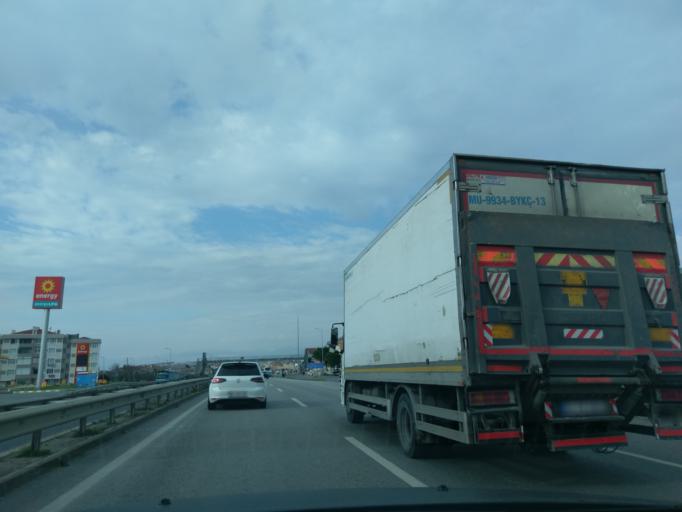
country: TR
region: Istanbul
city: Selimpasa
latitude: 41.0499
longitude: 28.3924
